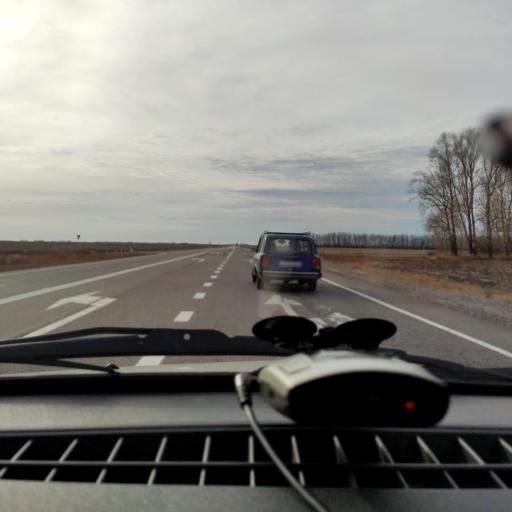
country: RU
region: Voronezj
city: Strelitsa
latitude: 51.4804
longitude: 38.9618
